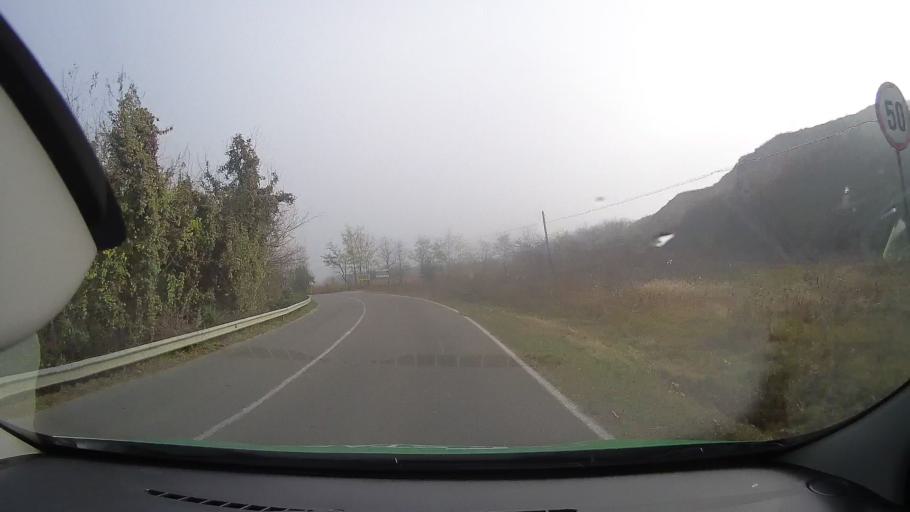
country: RO
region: Tulcea
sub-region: Comuna Nufaru
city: Nufaru
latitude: 45.1474
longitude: 28.9128
